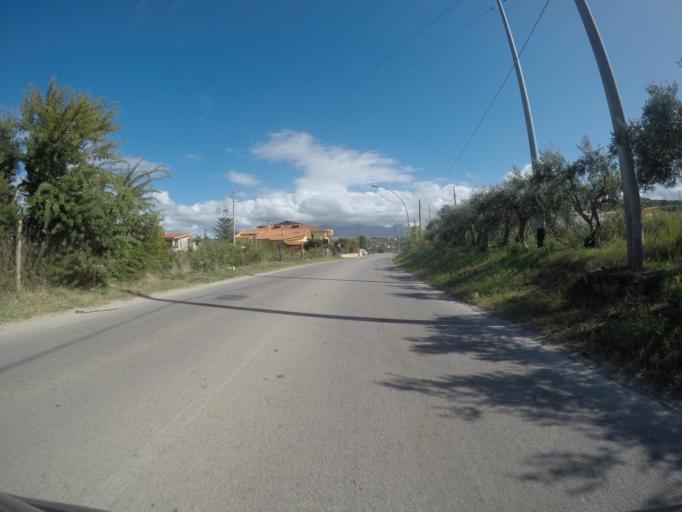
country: IT
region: Sicily
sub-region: Palermo
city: Trappeto
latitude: 38.0706
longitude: 13.0505
